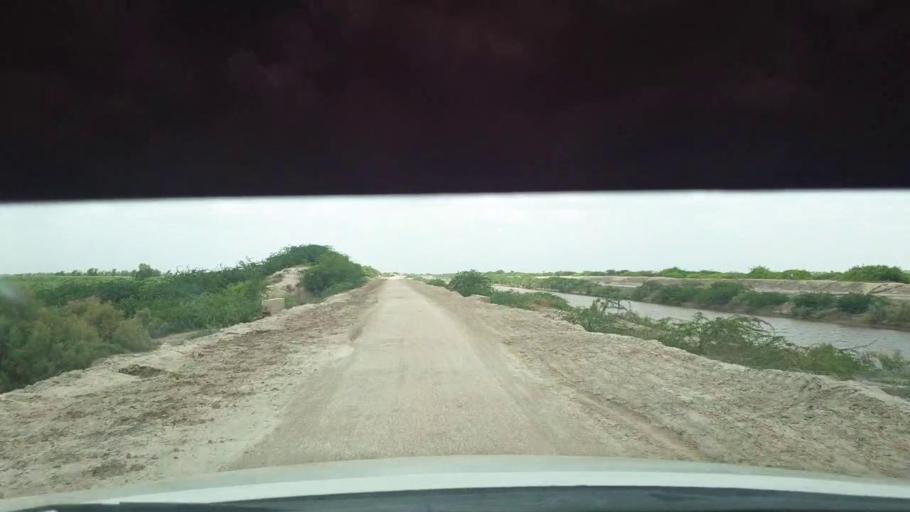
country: PK
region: Sindh
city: Kadhan
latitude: 24.5086
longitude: 69.1186
